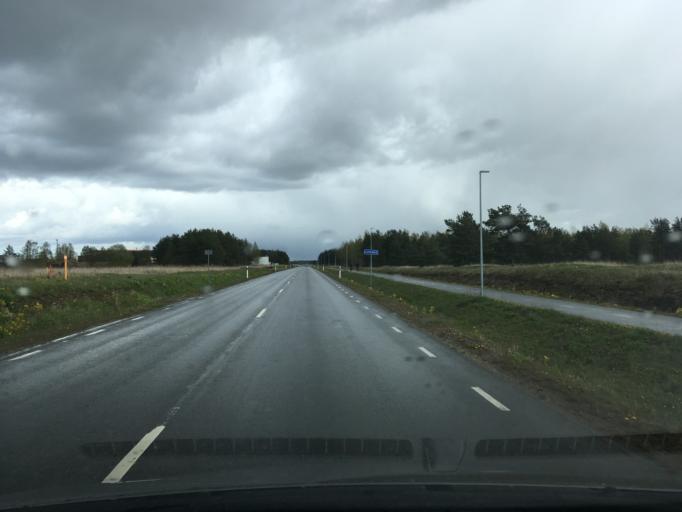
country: EE
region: Harju
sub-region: Joelaehtme vald
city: Loo
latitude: 59.4457
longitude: 24.9359
